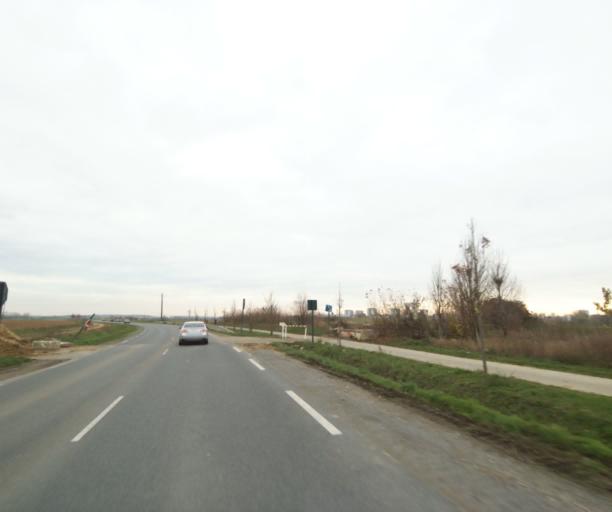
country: FR
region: Ile-de-France
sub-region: Departement du Val-d'Oise
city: Villiers-le-Bel
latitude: 49.0112
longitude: 2.4182
